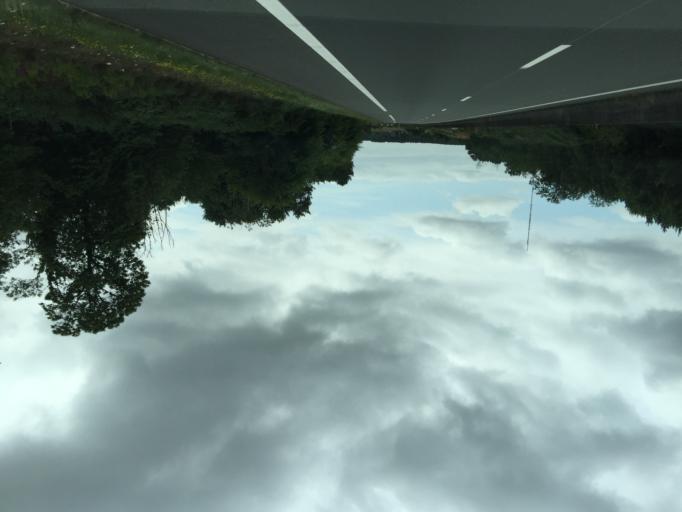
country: FR
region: Pays de la Loire
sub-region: Departement de la Sarthe
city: Mayet
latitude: 47.7801
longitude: 0.3113
